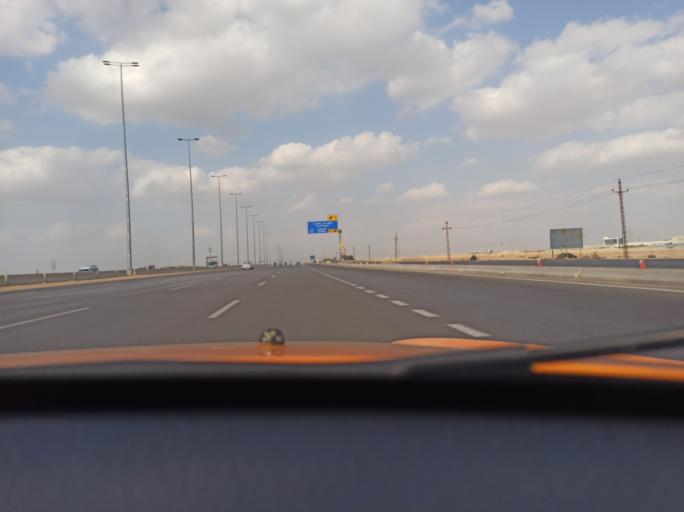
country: EG
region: Eastern Province
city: Bilbays
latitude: 30.2330
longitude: 31.7090
